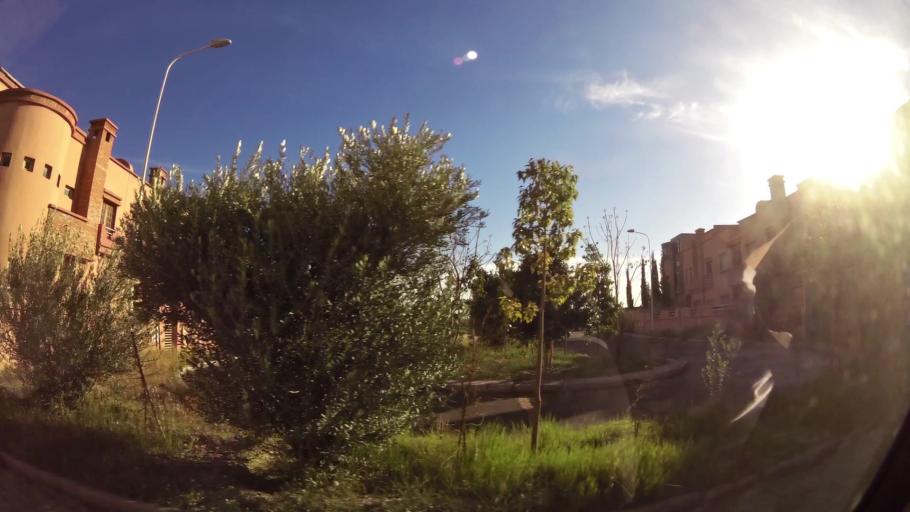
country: MA
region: Marrakech-Tensift-Al Haouz
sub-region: Marrakech
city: Marrakesh
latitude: 31.7583
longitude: -8.1061
